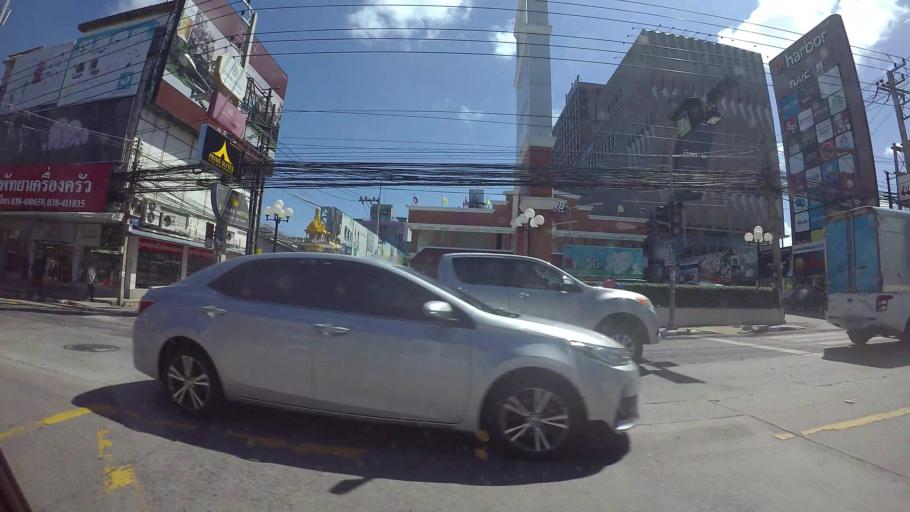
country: TH
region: Chon Buri
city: Phatthaya
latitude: 12.9332
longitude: 100.8968
